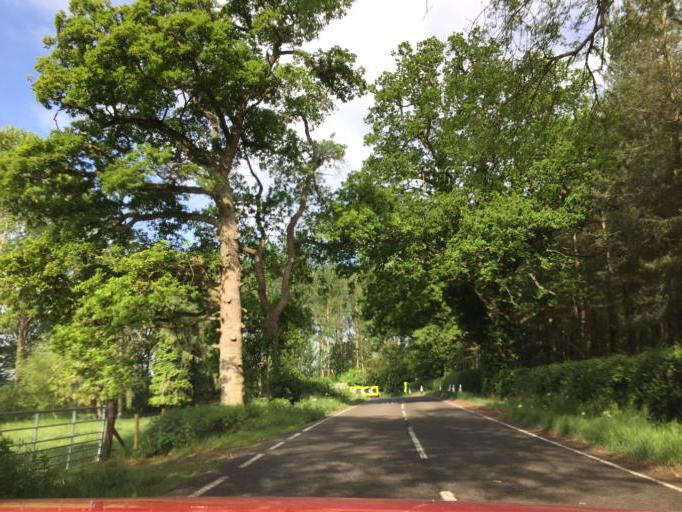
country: GB
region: England
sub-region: Northamptonshire
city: Towcester
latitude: 52.1333
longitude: -0.9558
